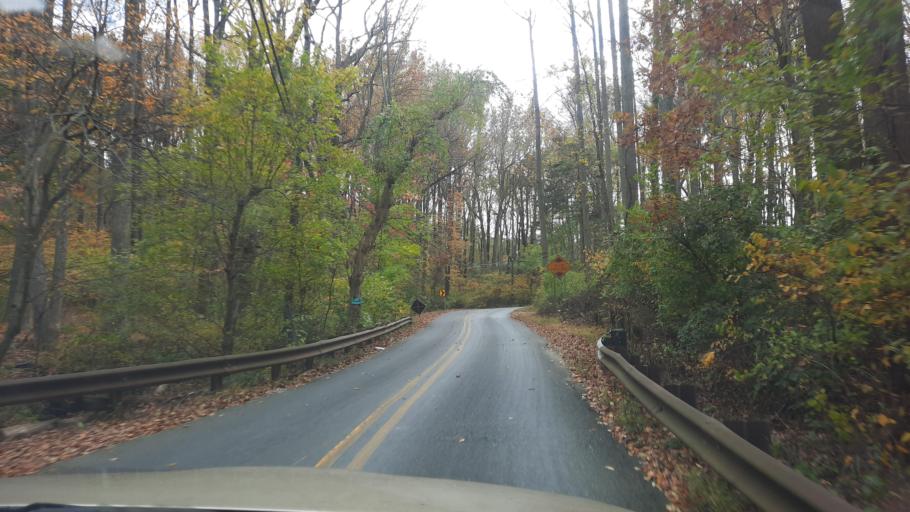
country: US
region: Maryland
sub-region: Montgomery County
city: Germantown
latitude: 39.1556
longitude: -77.2380
